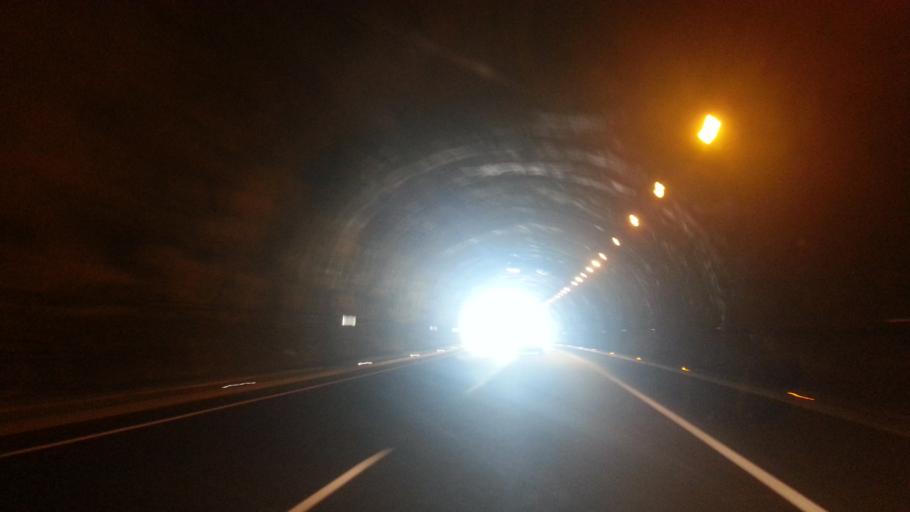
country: ES
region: Catalonia
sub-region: Provincia de Barcelona
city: Sant Pere de Ribes
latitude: 41.2738
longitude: 1.7324
